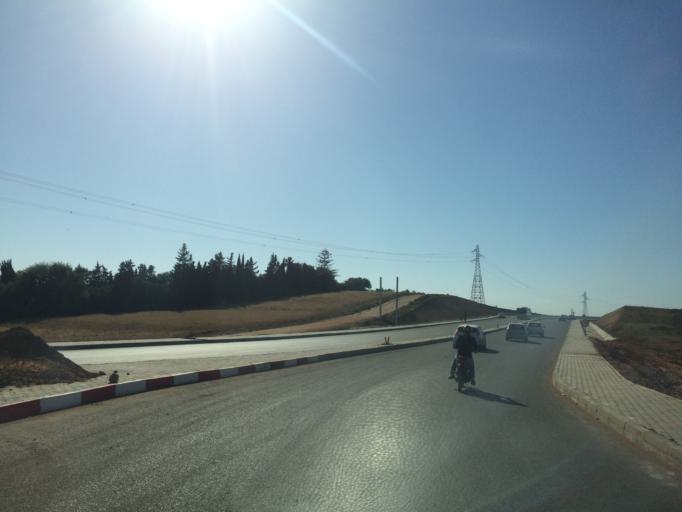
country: MA
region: Rabat-Sale-Zemmour-Zaer
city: Sale
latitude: 33.9786
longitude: -6.7386
